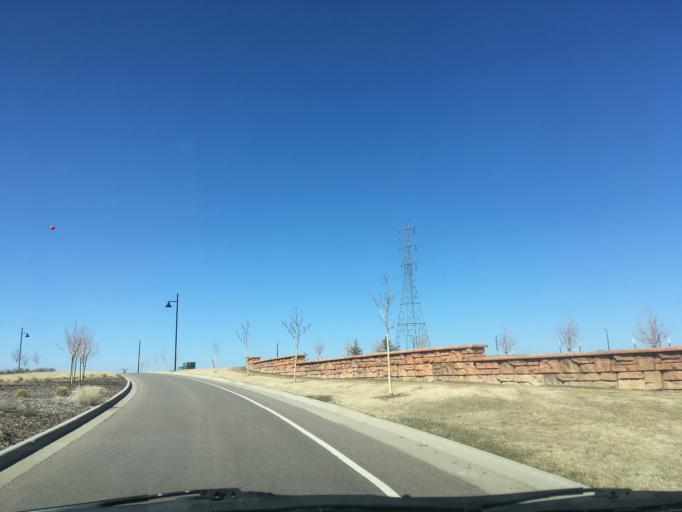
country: US
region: Colorado
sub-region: Boulder County
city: Erie
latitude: 40.0566
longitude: -105.0253
